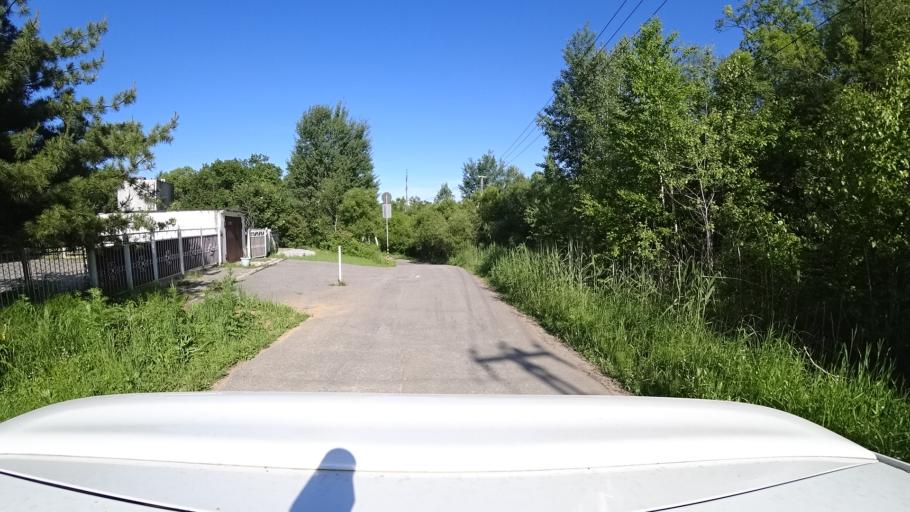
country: RU
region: Khabarovsk Krai
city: Topolevo
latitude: 48.5459
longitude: 135.1830
